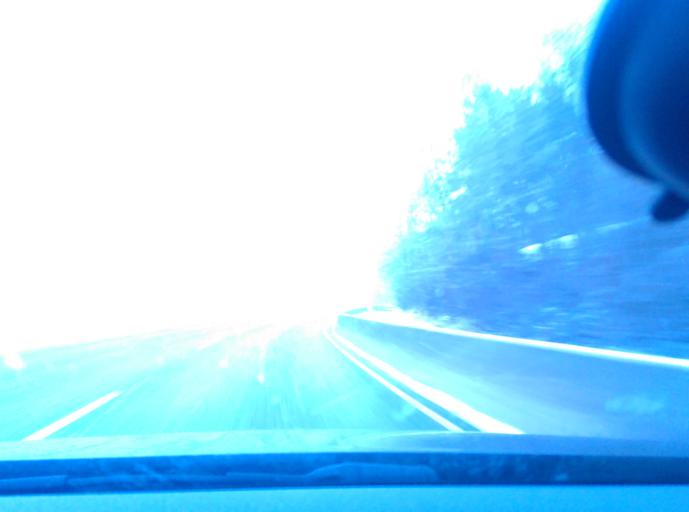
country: DE
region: Hesse
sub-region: Regierungsbezirk Kassel
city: Sontra
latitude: 51.0565
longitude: 10.0040
